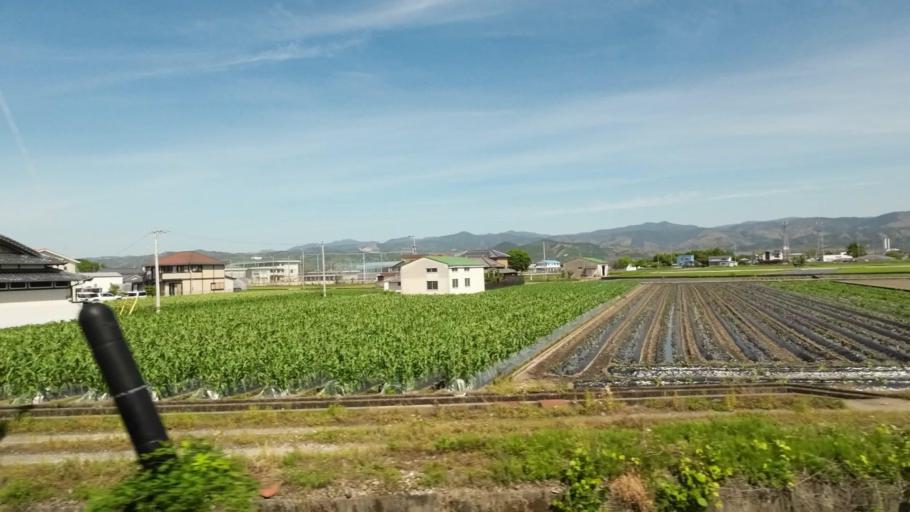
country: JP
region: Kochi
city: Kochi-shi
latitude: 33.5846
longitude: 133.6539
